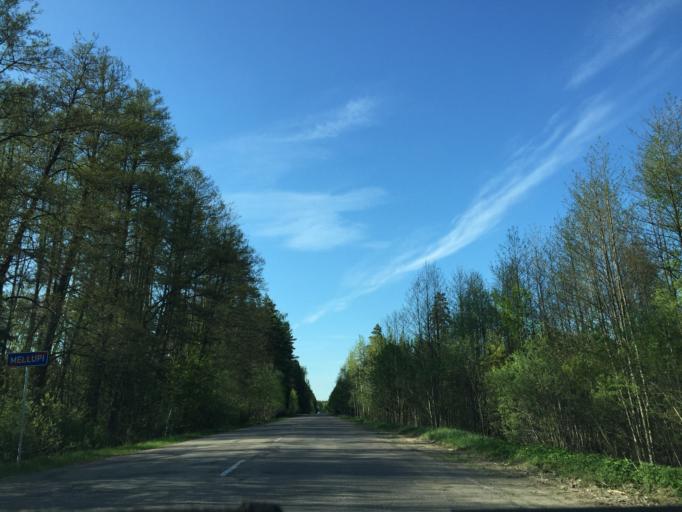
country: LV
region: Kekava
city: Balozi
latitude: 56.7390
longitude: 24.1088
